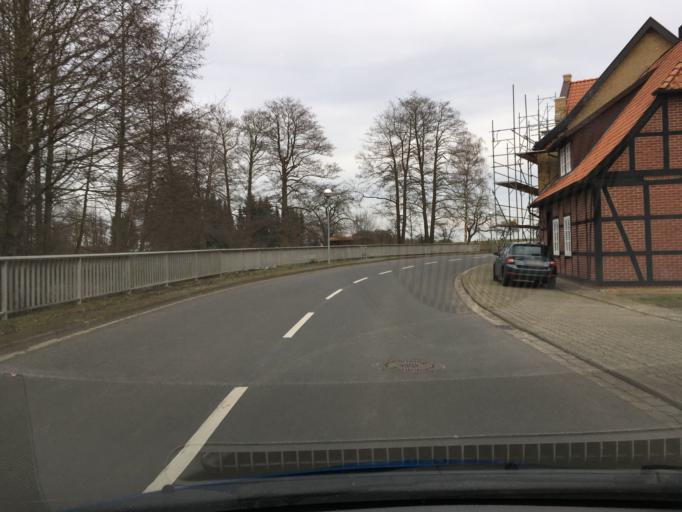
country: DE
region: Lower Saxony
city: Emmendorf
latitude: 53.0045
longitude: 10.6121
